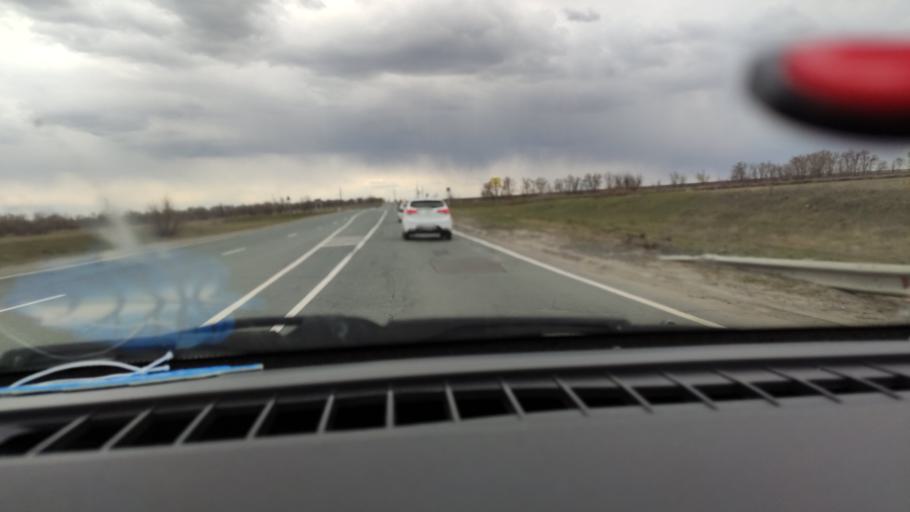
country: RU
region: Saratov
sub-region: Saratovskiy Rayon
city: Saratov
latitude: 51.7519
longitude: 46.0611
